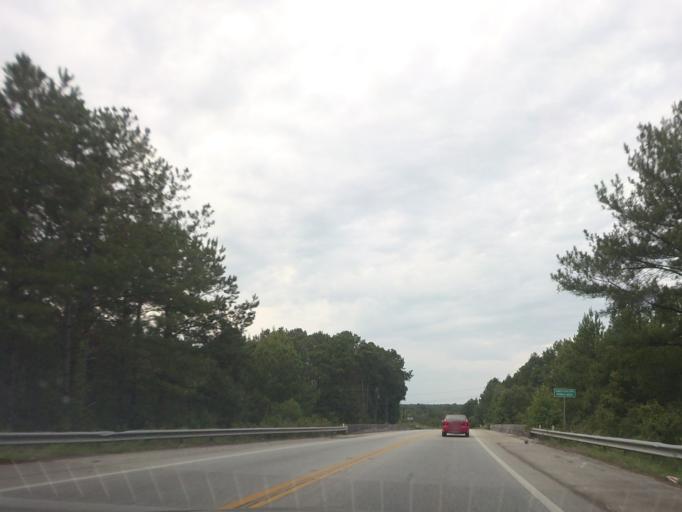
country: US
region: Georgia
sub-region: Bibb County
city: Macon
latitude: 32.8009
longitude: -83.5005
